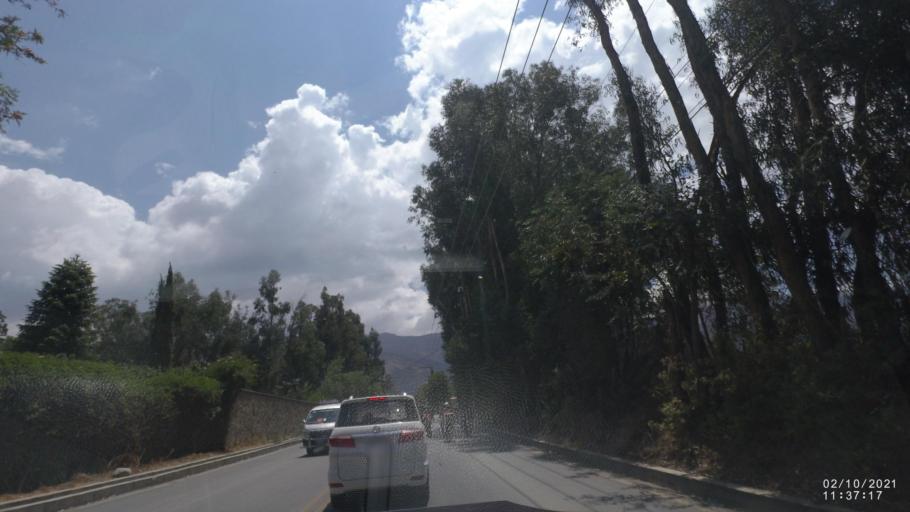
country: BO
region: Cochabamba
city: Cochabamba
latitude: -17.3440
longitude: -66.2227
